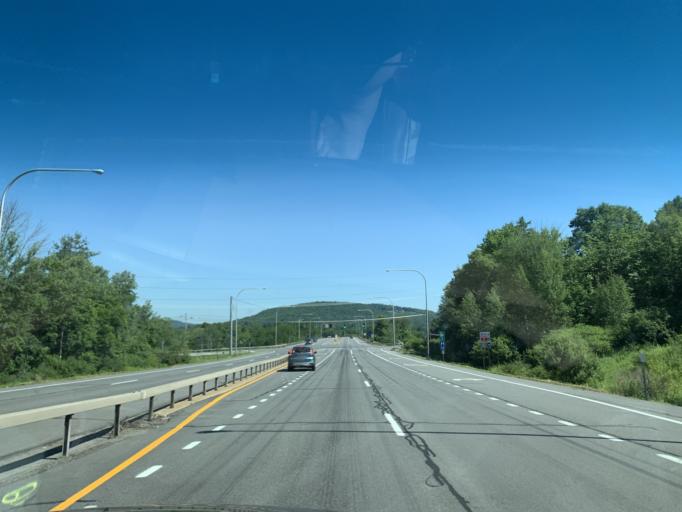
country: US
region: New York
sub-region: Delaware County
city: Sidney
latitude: 42.3011
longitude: -75.4045
